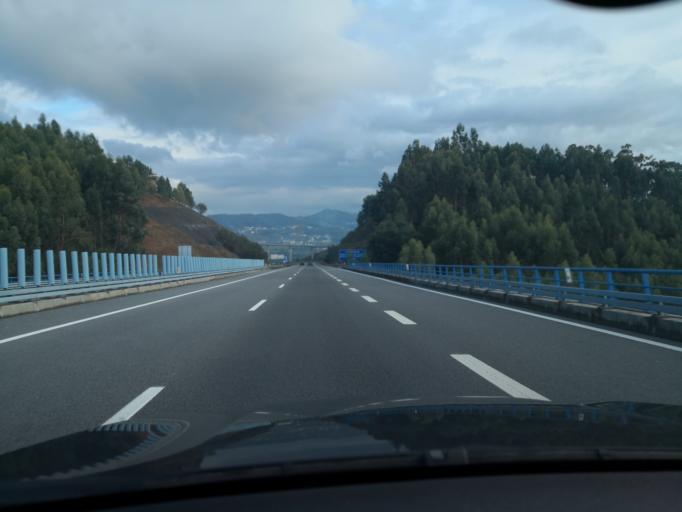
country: PT
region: Porto
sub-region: Felgueiras
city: Vizela
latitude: 41.4001
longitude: -8.2482
